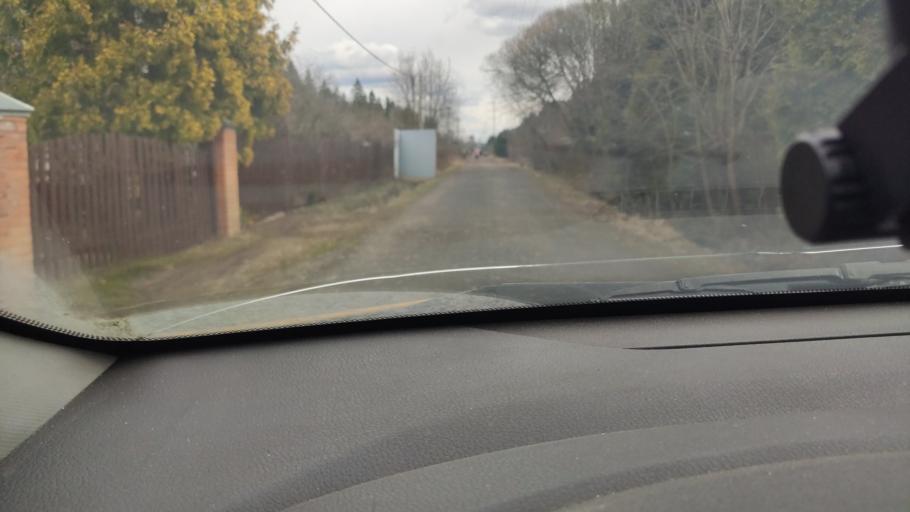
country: RU
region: Moskovskaya
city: Chupryakovo
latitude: 55.5829
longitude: 36.6075
